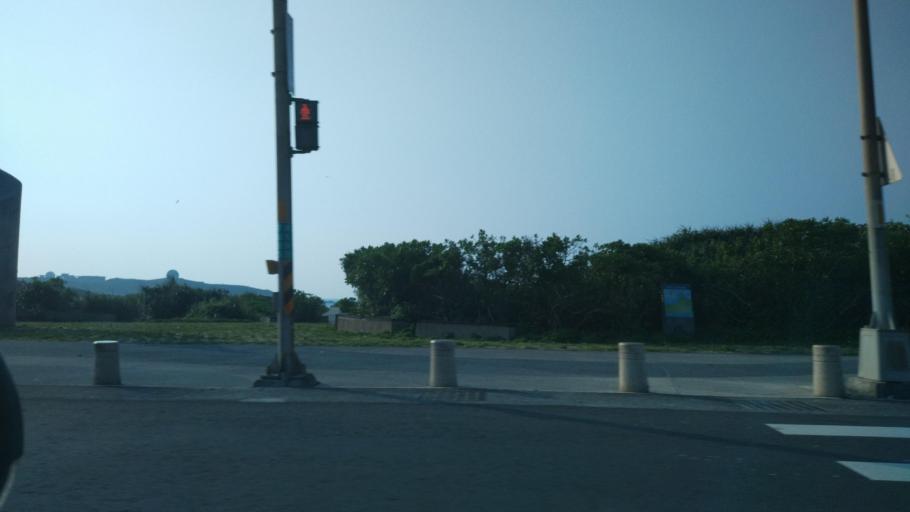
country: TW
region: Taipei
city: Taipei
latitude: 25.2897
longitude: 121.5490
